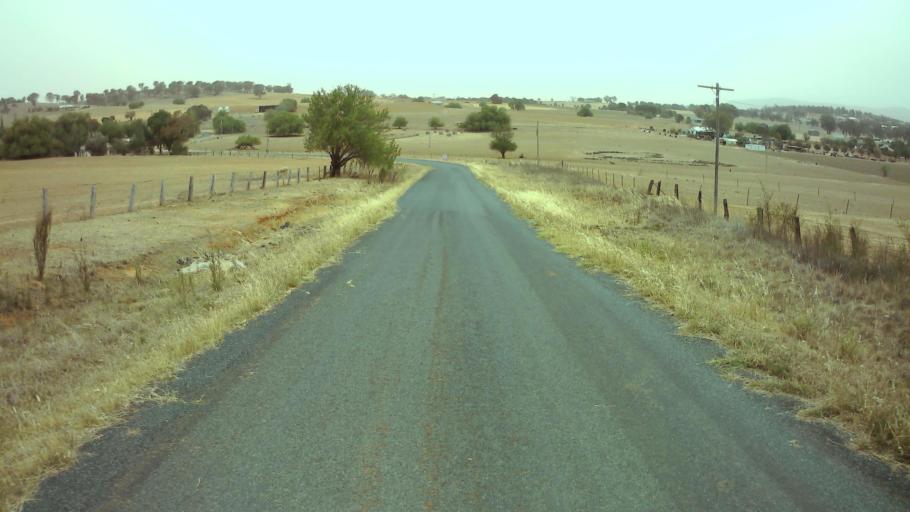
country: AU
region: New South Wales
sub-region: Weddin
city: Grenfell
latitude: -33.9030
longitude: 148.1696
